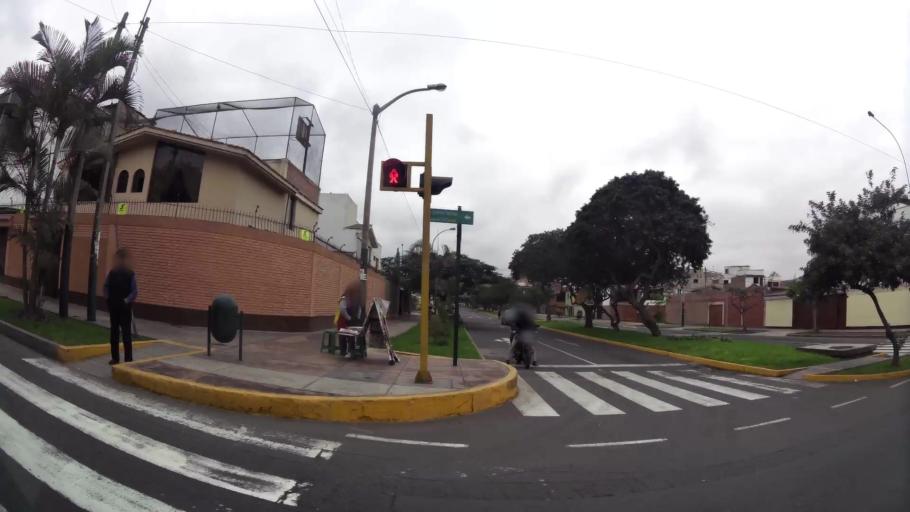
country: PE
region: Lima
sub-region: Lima
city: Surco
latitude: -12.1377
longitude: -76.9841
